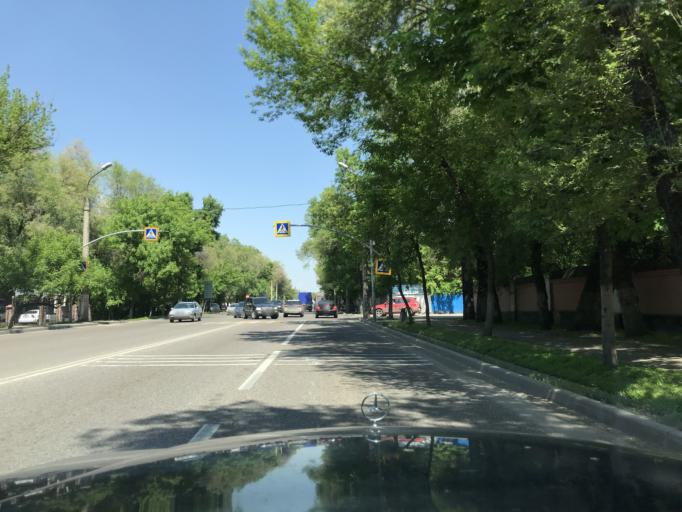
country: KZ
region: Almaty Oblysy
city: Pervomayskiy
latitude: 43.3283
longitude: 76.9597
